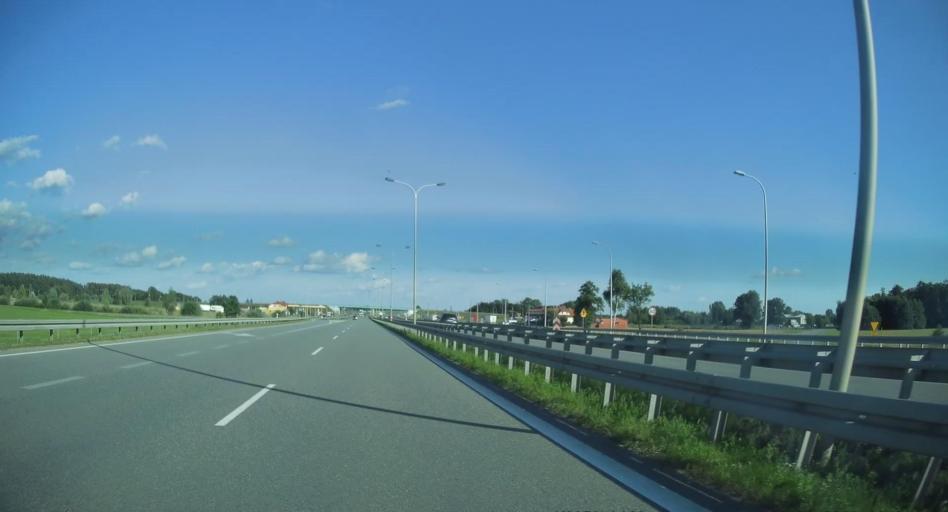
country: PL
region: Masovian Voivodeship
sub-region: Powiat bialobrzeski
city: Stara Blotnica
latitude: 51.5727
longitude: 21.0161
